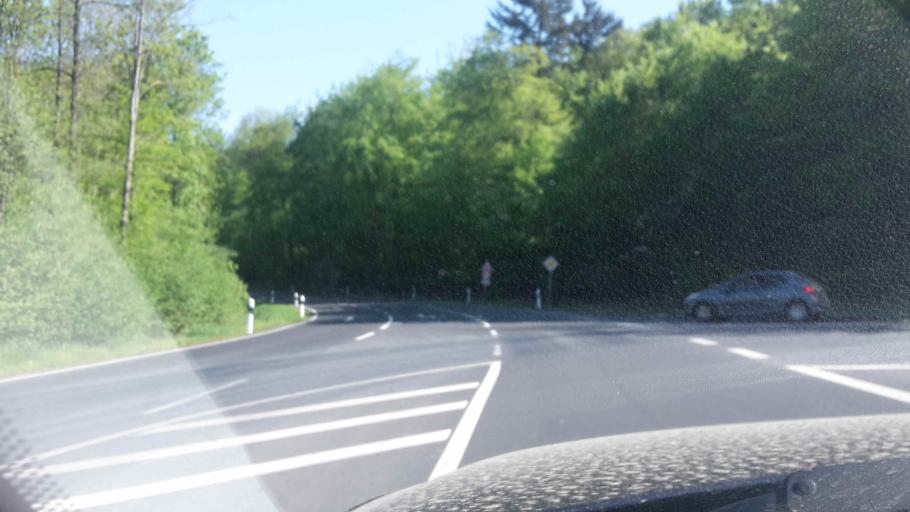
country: DE
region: Rheinland-Pfalz
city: Windhagen
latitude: 50.6958
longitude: 7.3218
